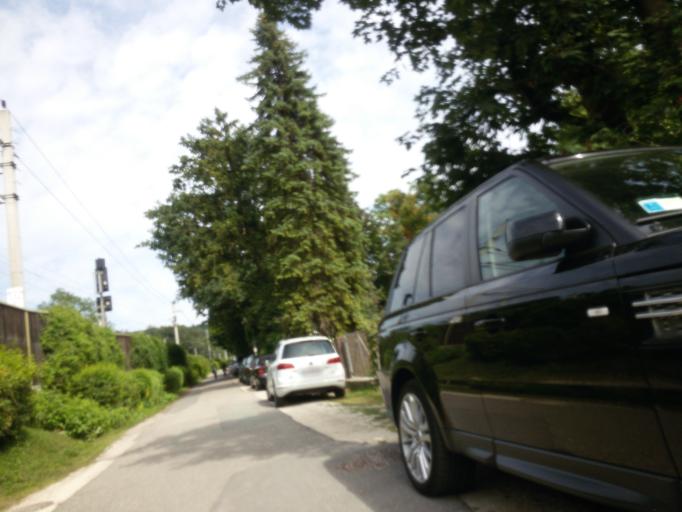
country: AT
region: Carinthia
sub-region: Politischer Bezirk Klagenfurt Land
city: Keutschach am See
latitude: 46.6277
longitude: 14.2313
